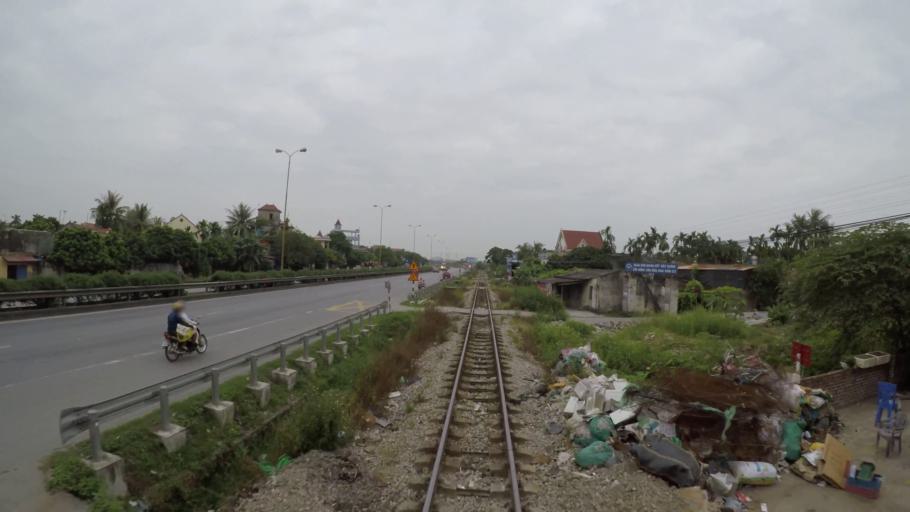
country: VN
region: Hai Duong
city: Phu Thai
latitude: 20.9539
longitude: 106.5297
